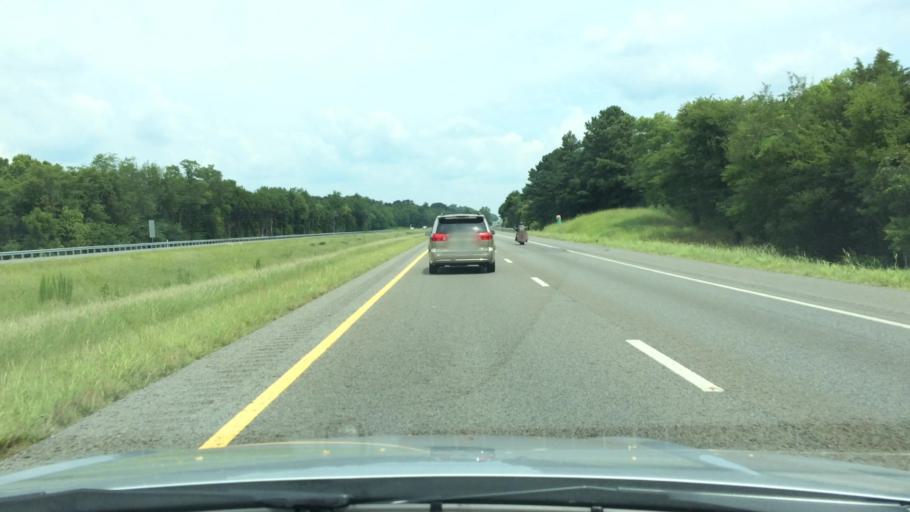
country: US
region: Tennessee
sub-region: Marshall County
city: Lewisburg
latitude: 35.4553
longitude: -86.8853
